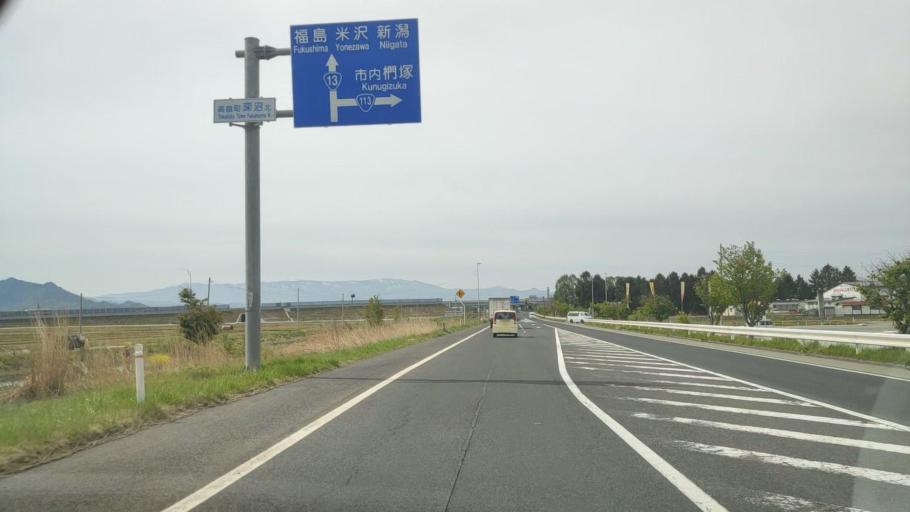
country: JP
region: Yamagata
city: Takahata
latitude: 38.0322
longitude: 140.1716
